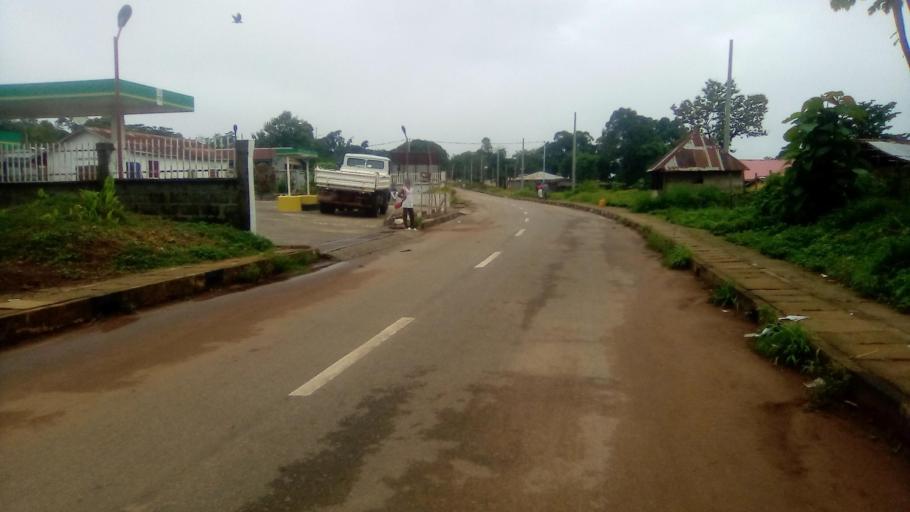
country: SL
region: Southern Province
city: Moyamba
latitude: 8.1627
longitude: -12.4391
